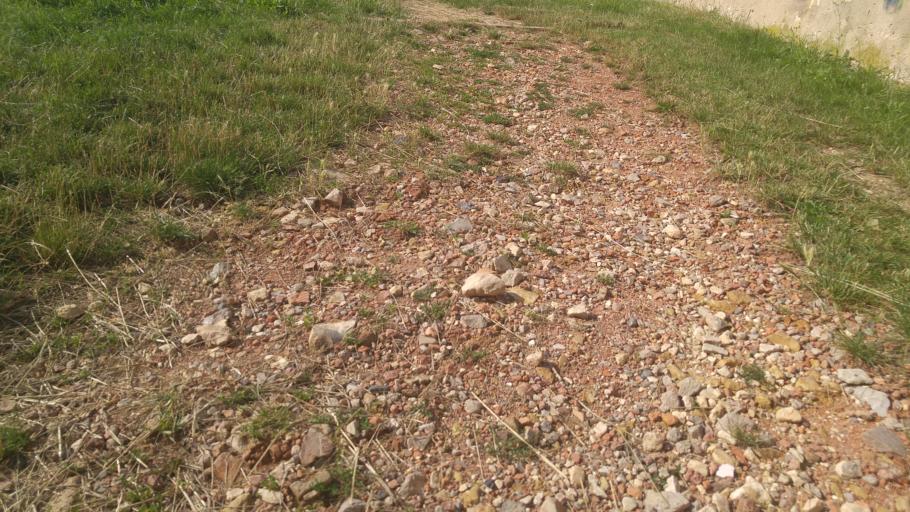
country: CZ
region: Praha
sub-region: Praha 1
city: Mala Strana
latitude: 50.0869
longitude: 14.3604
